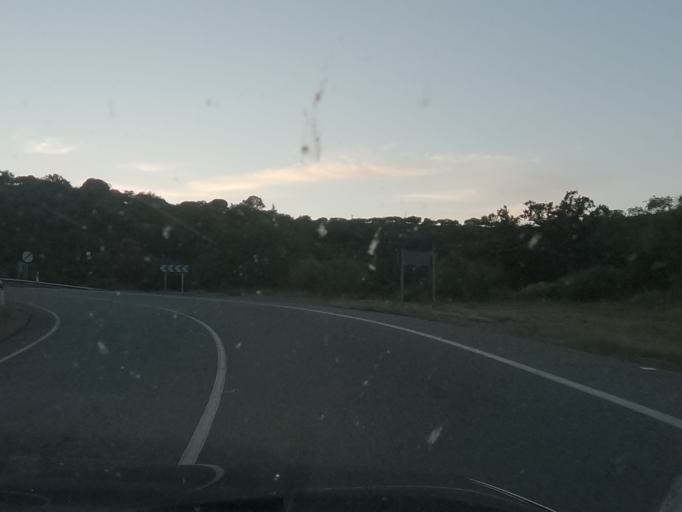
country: ES
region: Extremadura
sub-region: Provincia de Caceres
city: Alcantara
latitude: 39.7323
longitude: -6.8961
